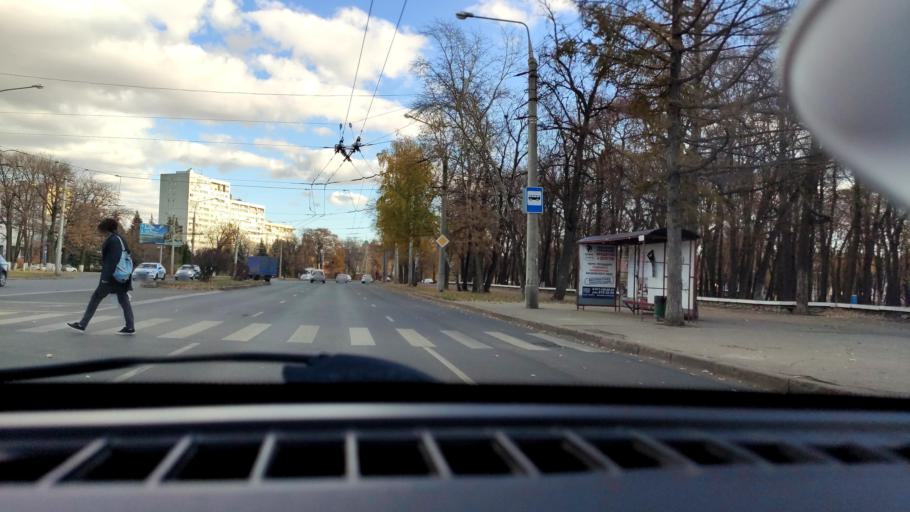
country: RU
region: Samara
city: Samara
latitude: 53.2317
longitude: 50.2016
